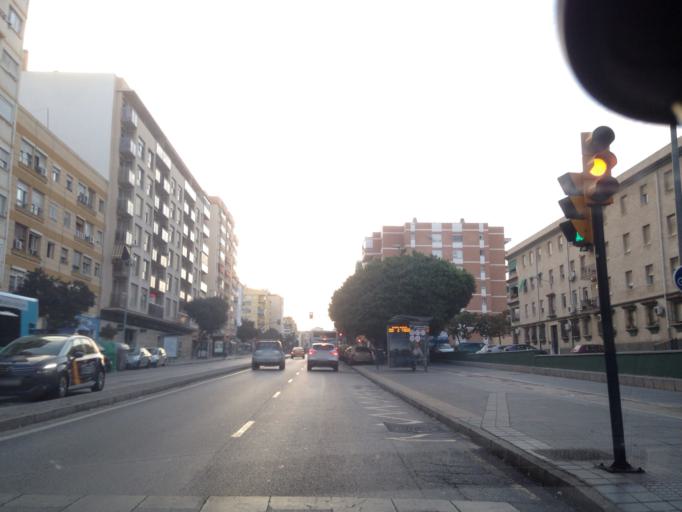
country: ES
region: Andalusia
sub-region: Provincia de Malaga
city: Malaga
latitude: 36.7215
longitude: -4.4359
